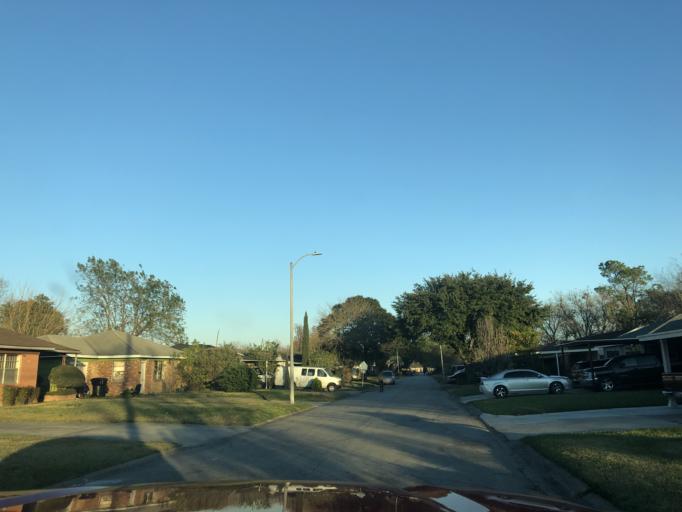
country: US
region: Texas
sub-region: Harris County
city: Jacinto City
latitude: 29.7641
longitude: -95.2698
